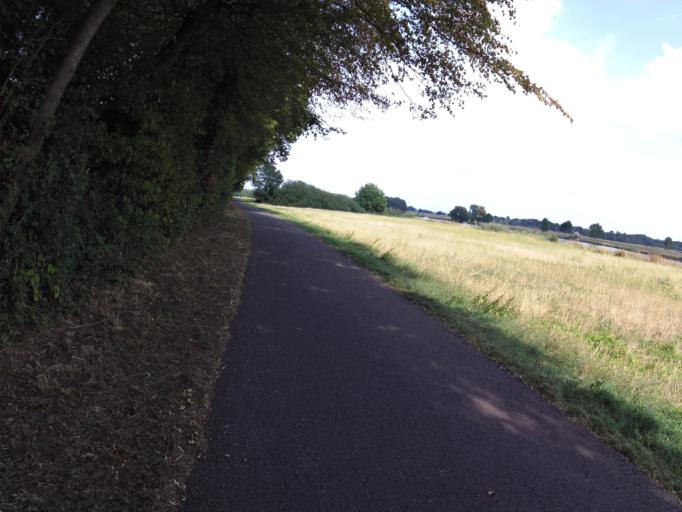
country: DE
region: North Rhine-Westphalia
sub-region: Regierungsbezirk Detmold
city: Petershagen
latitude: 52.3461
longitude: 8.9482
